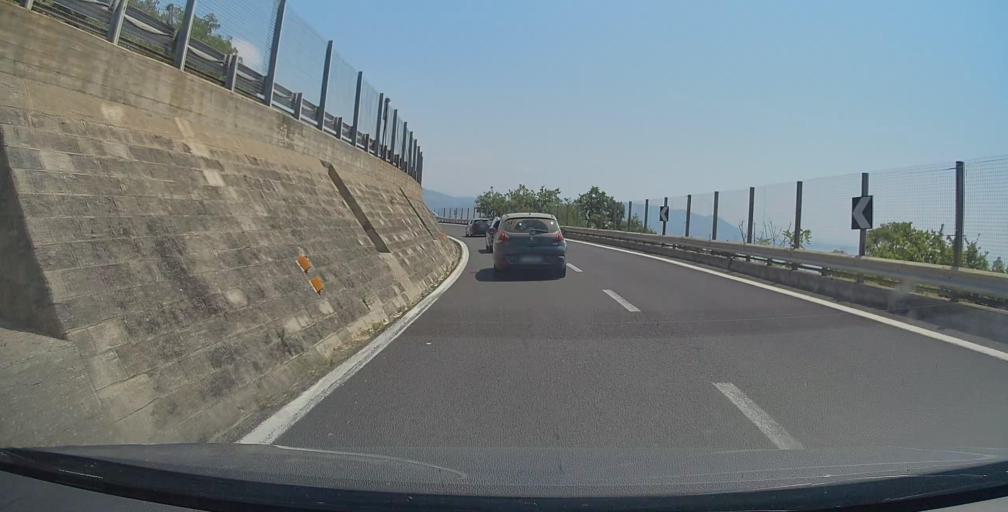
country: IT
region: Campania
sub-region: Provincia di Salerno
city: Vietri sul Mare
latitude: 40.6731
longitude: 14.7323
